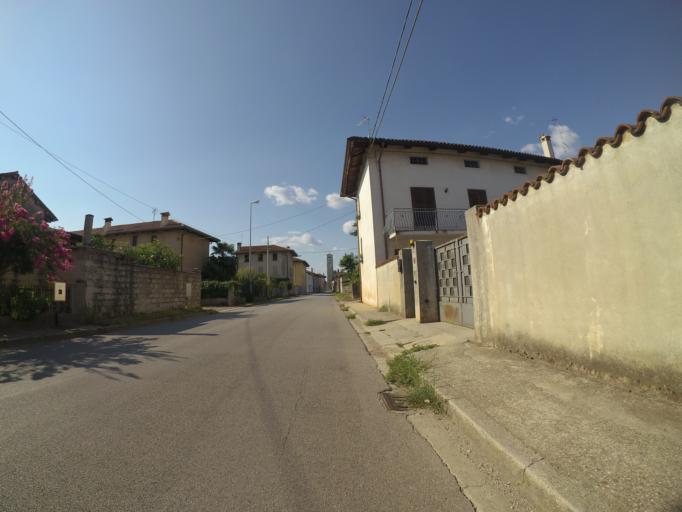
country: IT
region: Friuli Venezia Giulia
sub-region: Provincia di Udine
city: Lestizza
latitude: 45.9692
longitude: 13.1598
